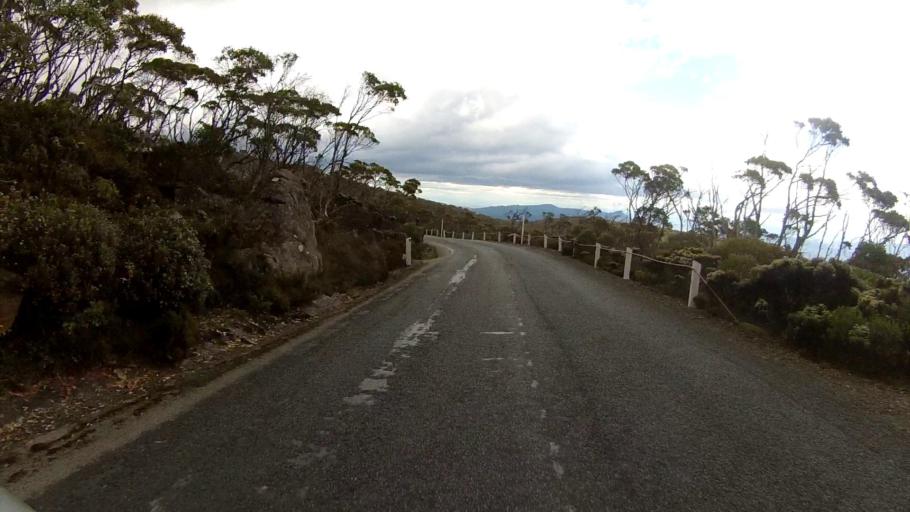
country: AU
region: Tasmania
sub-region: Glenorchy
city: West Moonah
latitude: -42.8912
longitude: 147.2242
